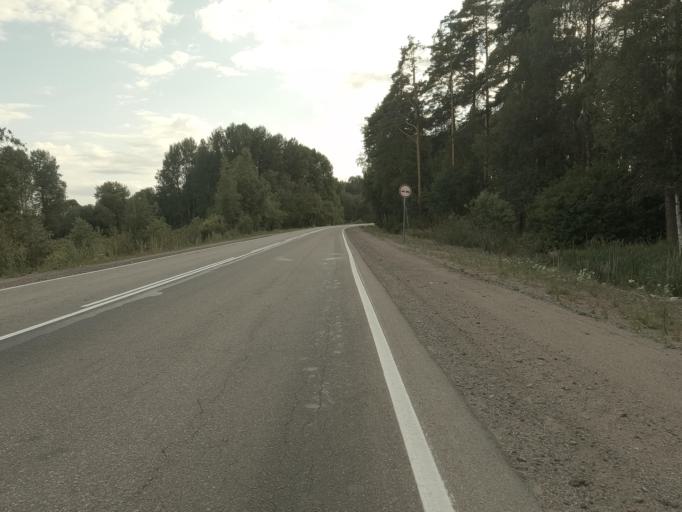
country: RU
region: Leningrad
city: Kamennogorsk
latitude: 60.8728
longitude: 28.9945
